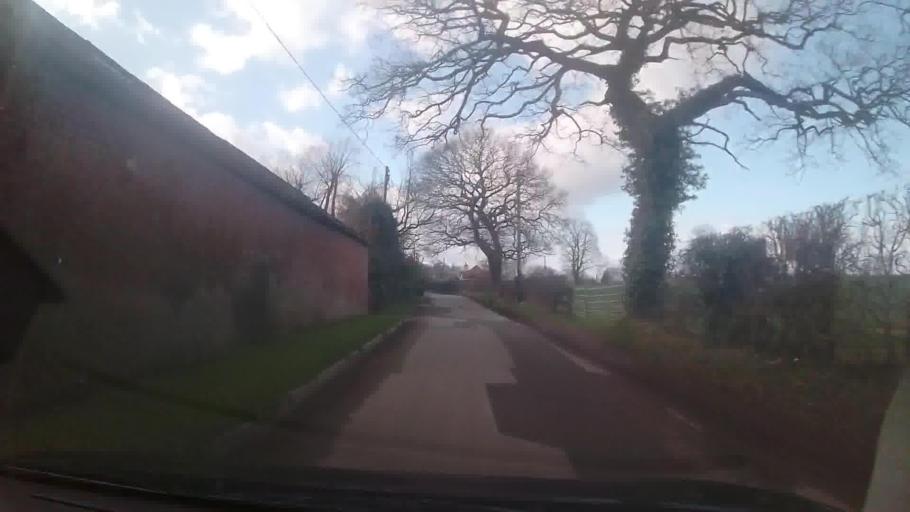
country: GB
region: England
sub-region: Shropshire
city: Ash
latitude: 52.9389
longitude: -2.6645
